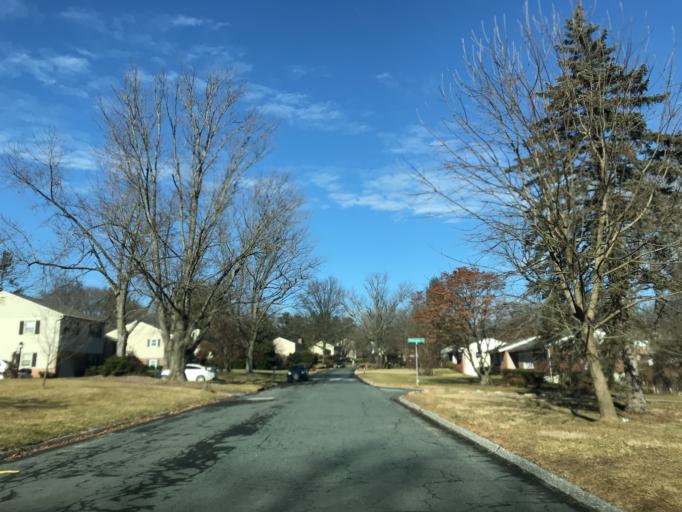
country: US
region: Maryland
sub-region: Baltimore County
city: Hampton
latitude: 39.4093
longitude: -76.5759
